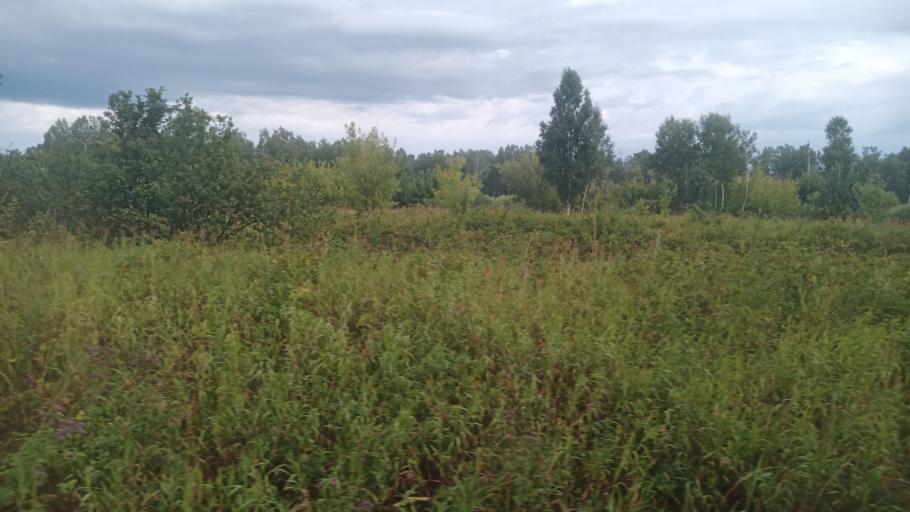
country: RU
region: Altai Krai
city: Nalobikha
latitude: 53.2279
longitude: 84.4999
